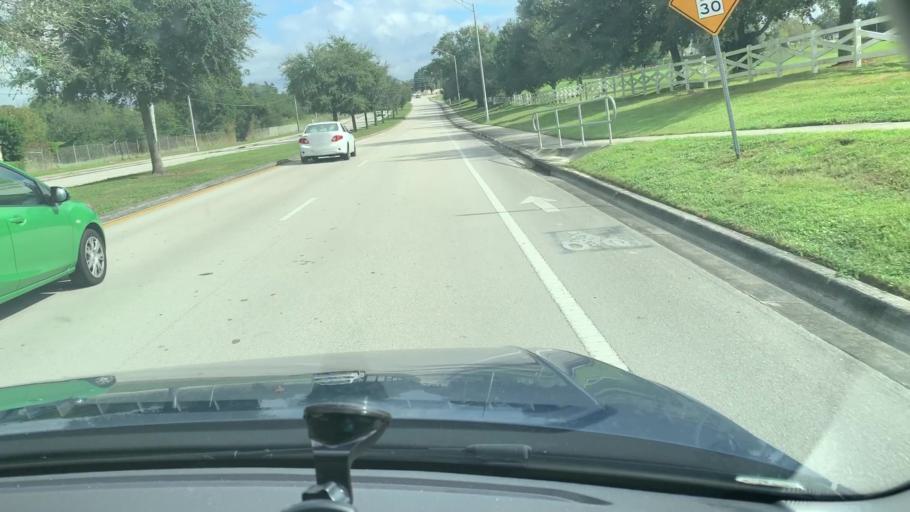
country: US
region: Florida
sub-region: Polk County
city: Gibsonia
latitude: 28.0931
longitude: -81.9834
